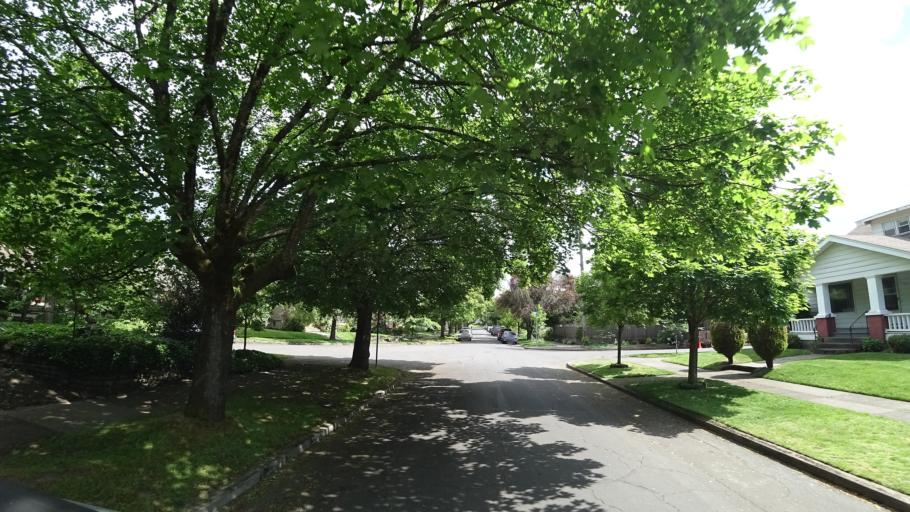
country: US
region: Oregon
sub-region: Multnomah County
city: Portland
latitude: 45.5076
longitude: -122.6466
